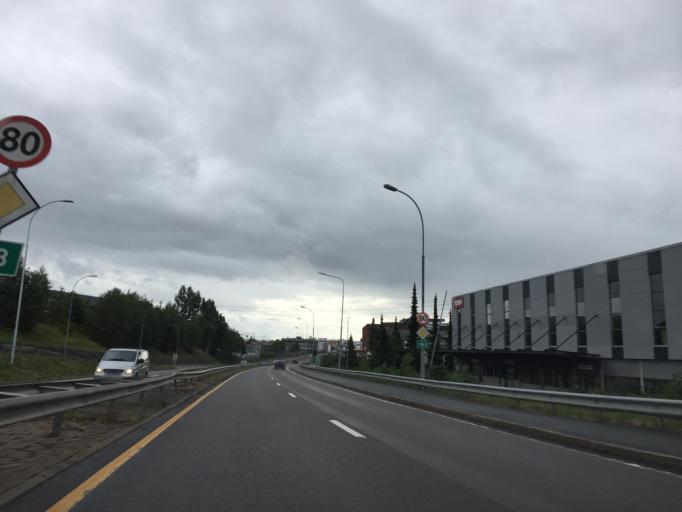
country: NO
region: Akershus
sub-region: Lorenskog
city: Kjenn
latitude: 59.9493
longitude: 10.8837
